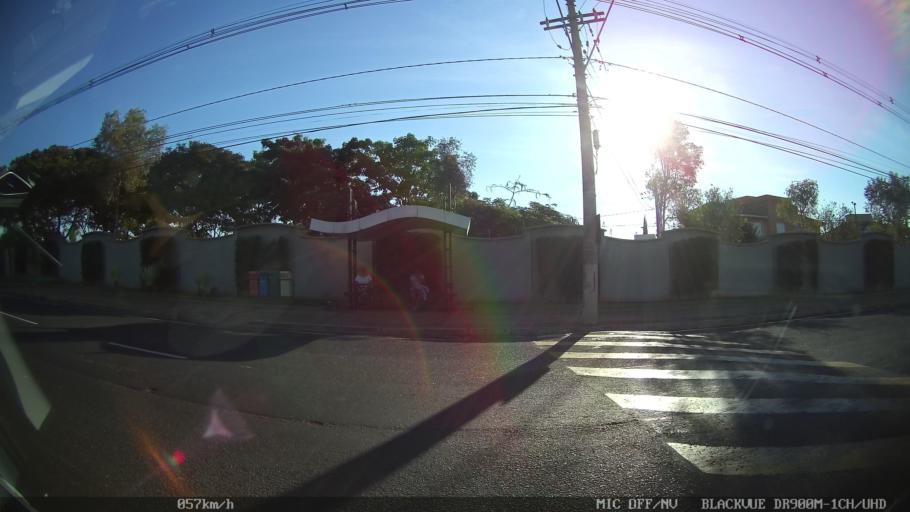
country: BR
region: Sao Paulo
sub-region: Sao Jose Do Rio Preto
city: Sao Jose do Rio Preto
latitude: -20.8592
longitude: -49.4123
